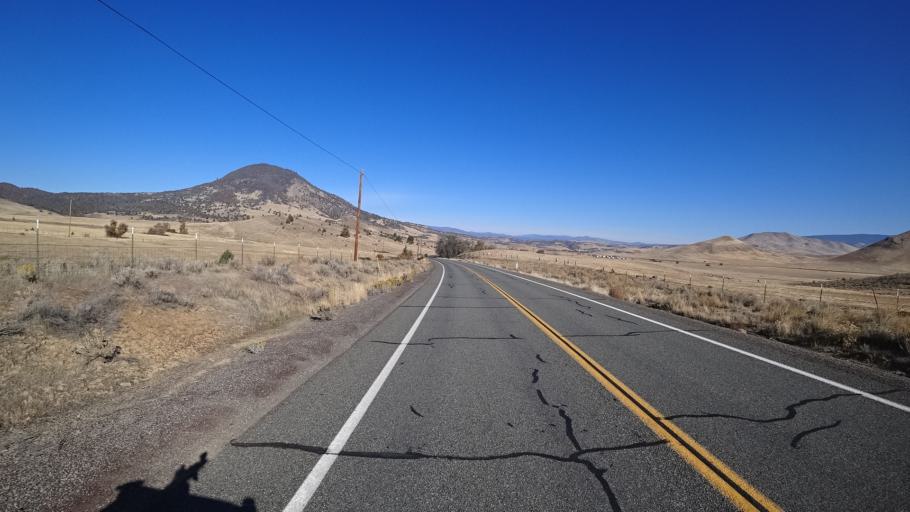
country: US
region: California
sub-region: Siskiyou County
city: Montague
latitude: 41.8159
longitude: -122.4973
